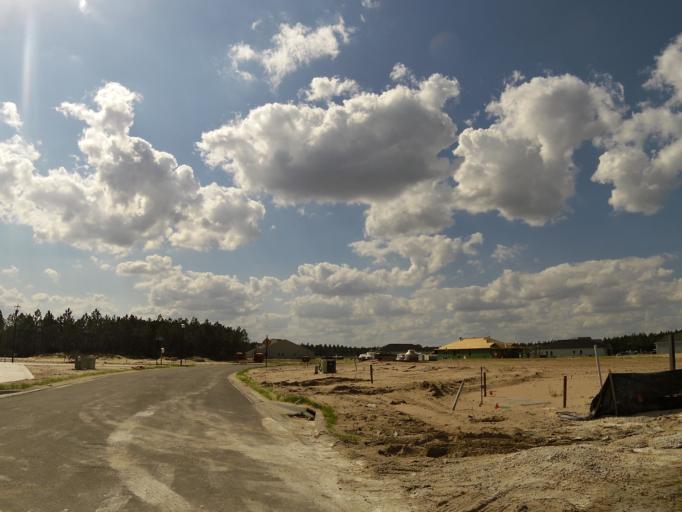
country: US
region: Florida
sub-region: Saint Johns County
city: Palm Valley
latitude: 30.1952
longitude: -81.5033
